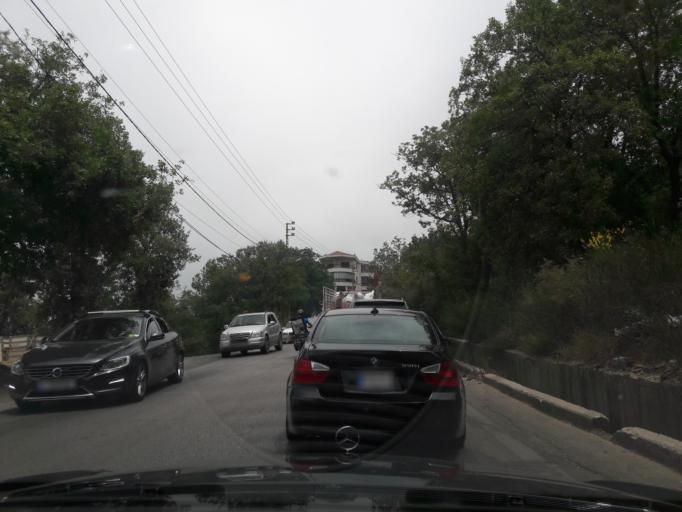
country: LB
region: Mont-Liban
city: Djounie
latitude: 33.9138
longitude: 35.6917
